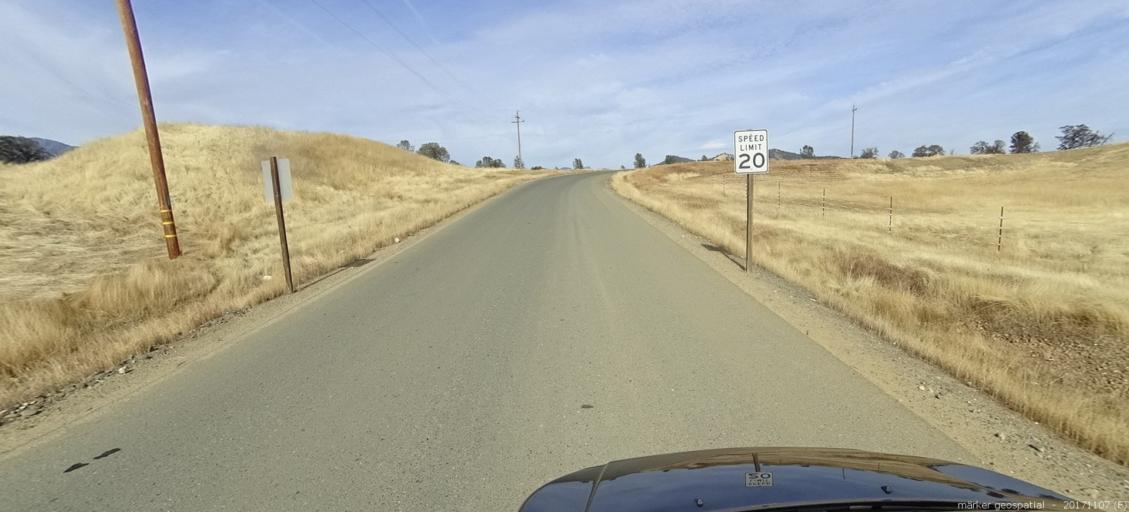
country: US
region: California
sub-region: Shasta County
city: Shasta
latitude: 40.4838
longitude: -122.5385
